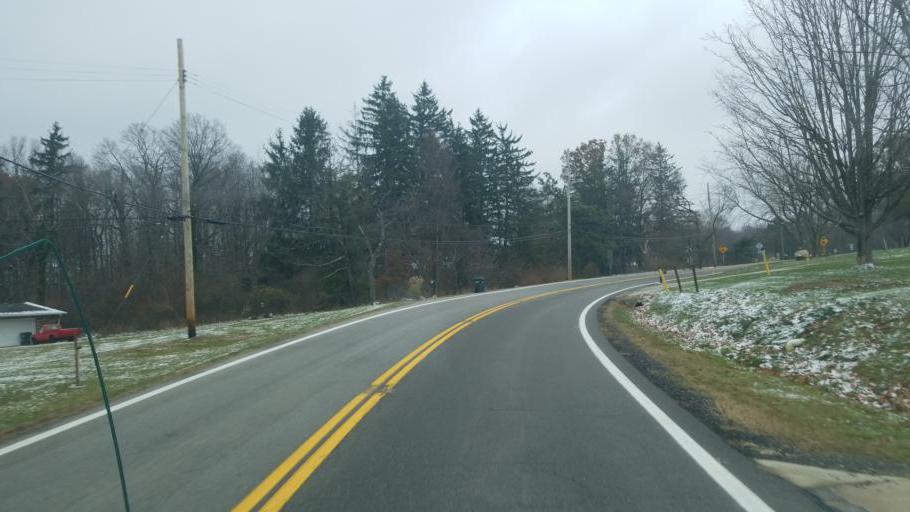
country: US
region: Ohio
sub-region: Cuyahoga County
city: North Royalton
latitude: 41.2767
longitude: -81.7208
